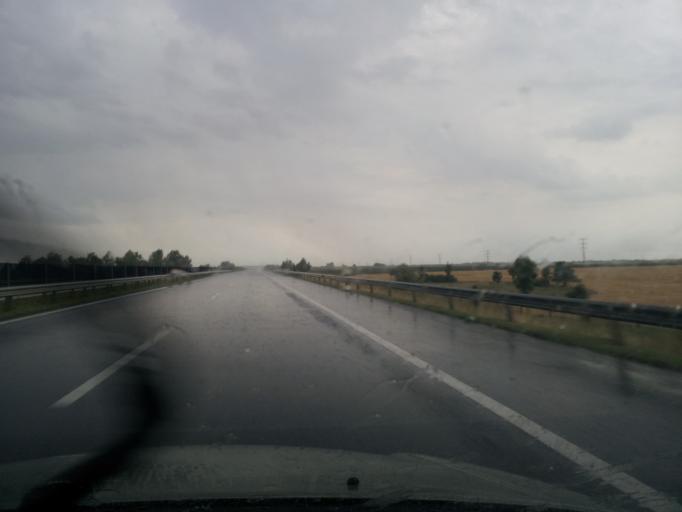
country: HU
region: Borsod-Abauj-Zemplen
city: Malyi
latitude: 48.0236
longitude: 20.8678
